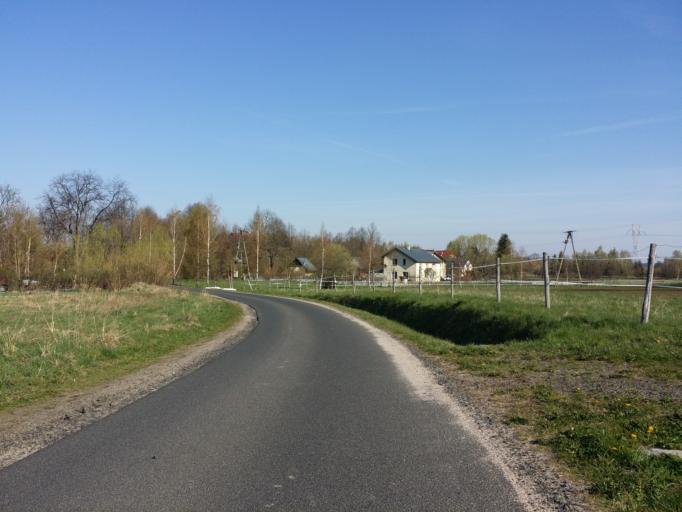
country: PL
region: Lower Silesian Voivodeship
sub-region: Powiat lwowecki
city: Mirsk
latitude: 50.9451
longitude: 15.4264
